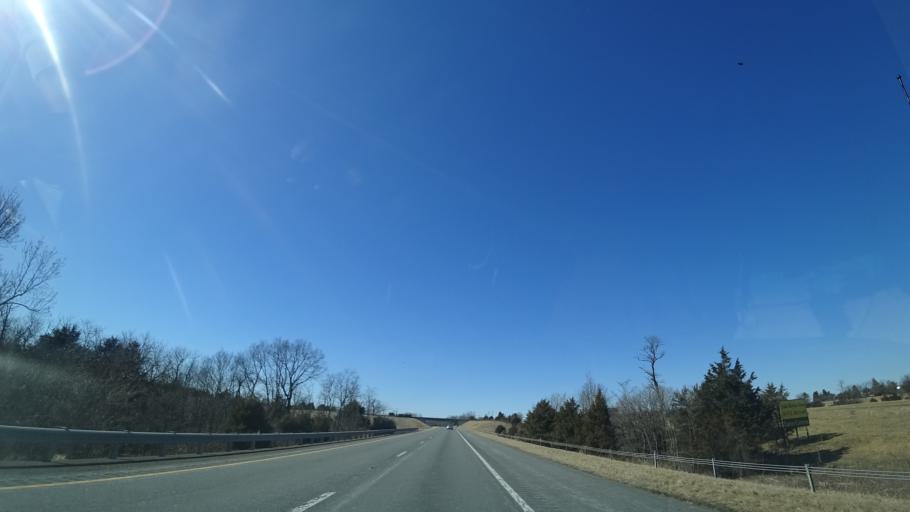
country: US
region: Virginia
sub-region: Warren County
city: Apple Mountain Lake
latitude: 38.9448
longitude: -78.1433
